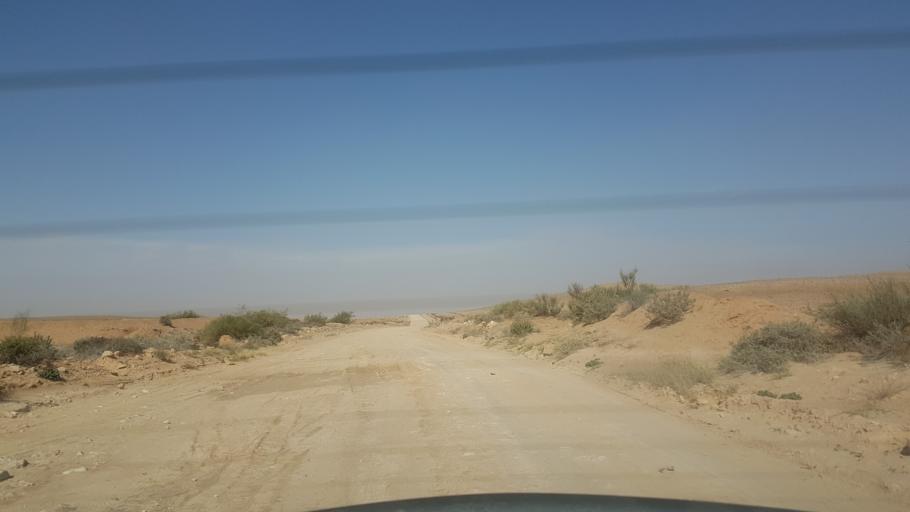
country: TN
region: Qabis
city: El Hamma
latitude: 33.6526
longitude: 9.7362
